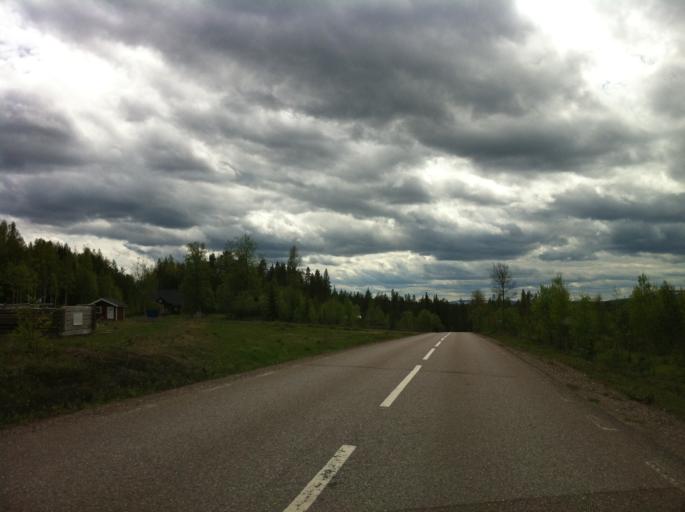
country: NO
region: Hedmark
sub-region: Trysil
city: Innbygda
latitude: 61.5153
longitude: 13.0841
